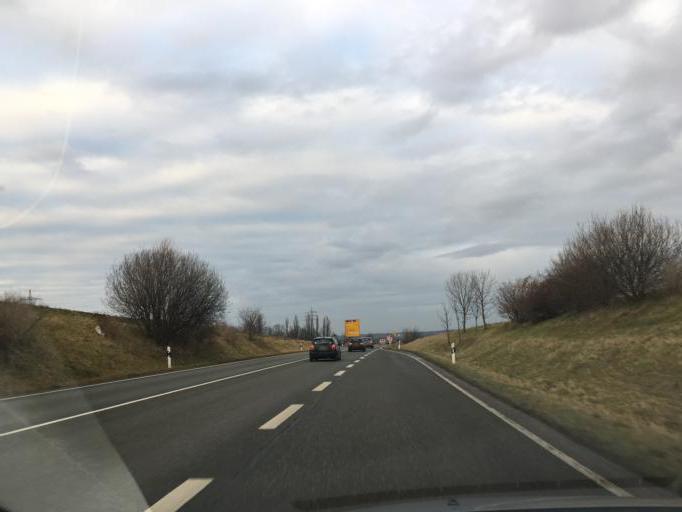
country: DE
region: Thuringia
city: Nobitz
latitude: 50.9867
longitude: 12.4664
